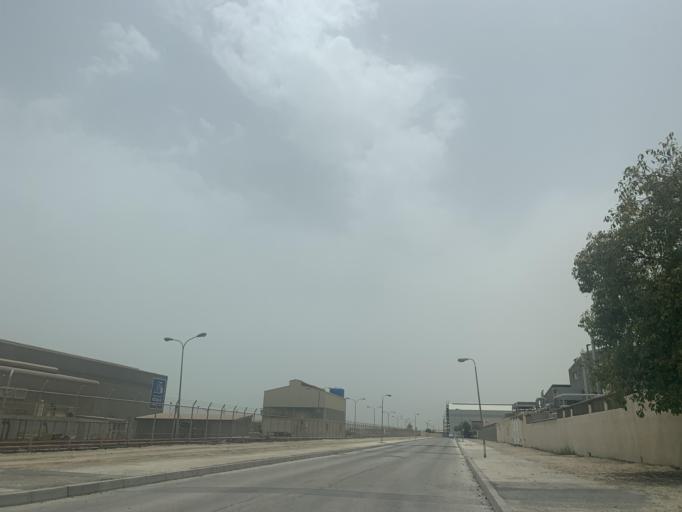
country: BH
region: Northern
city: Sitrah
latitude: 26.1819
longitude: 50.6127
